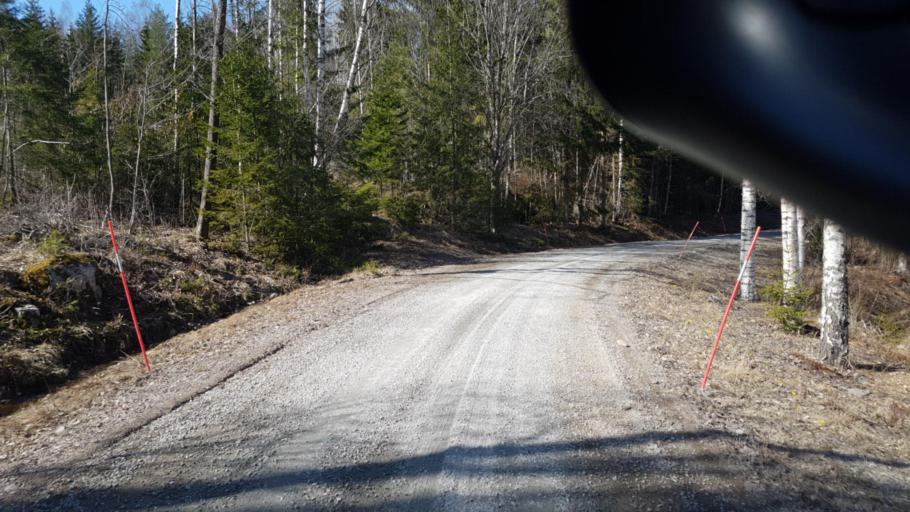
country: SE
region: Vaermland
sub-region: Arvika Kommun
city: Arvika
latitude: 59.5782
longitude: 12.8253
